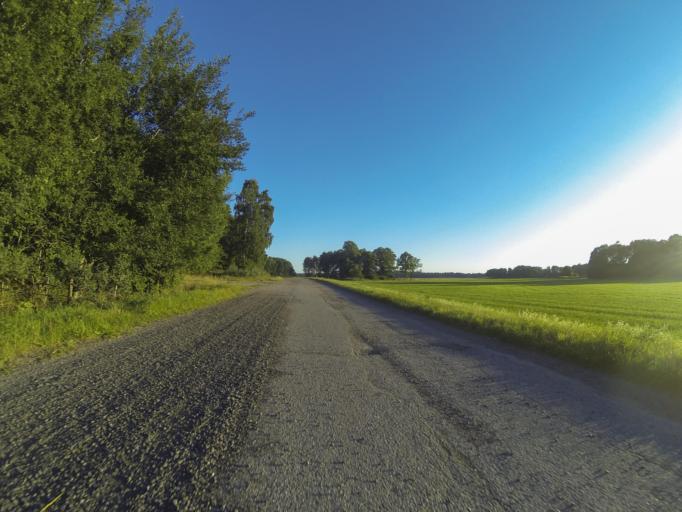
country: SE
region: Vaestmanland
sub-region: Vasteras
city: Vasteras
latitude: 59.5742
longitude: 16.6529
